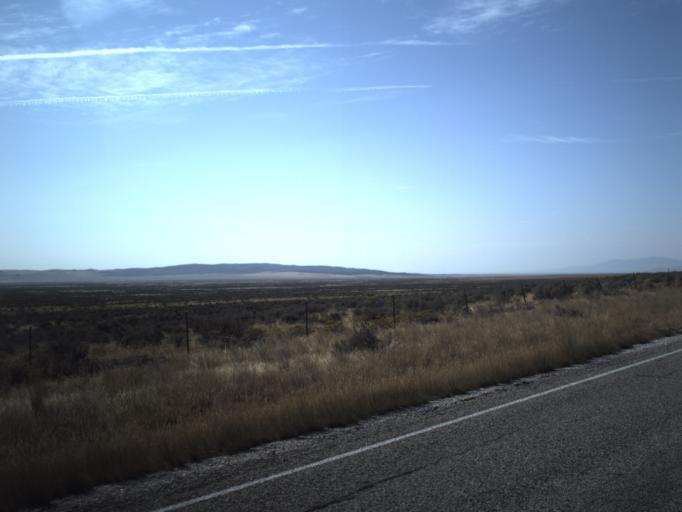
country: US
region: Idaho
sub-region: Oneida County
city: Malad City
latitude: 41.9435
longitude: -113.0825
